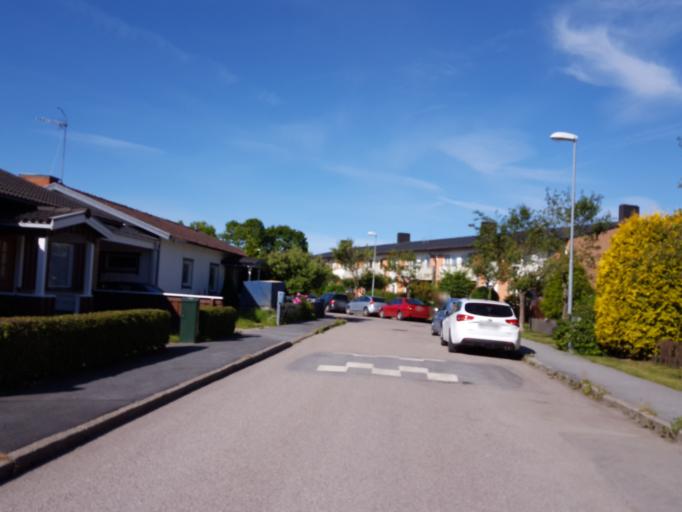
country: SE
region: Uppsala
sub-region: Uppsala Kommun
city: Uppsala
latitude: 59.8616
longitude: 17.6823
